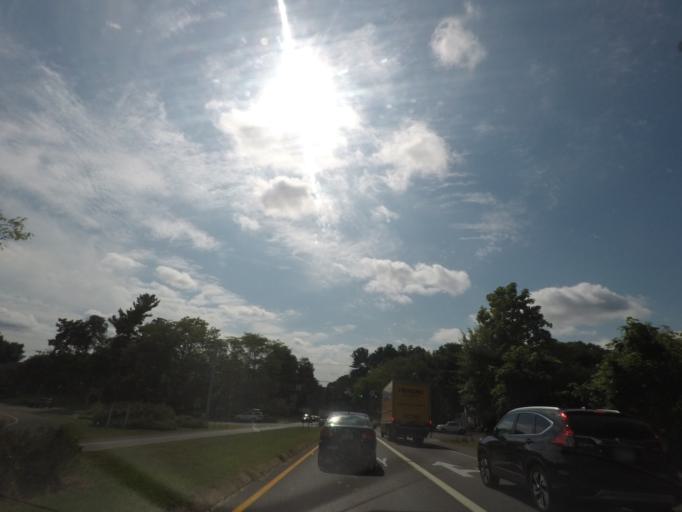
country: US
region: New York
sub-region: Albany County
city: Delmar
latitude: 42.6269
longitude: -73.8546
